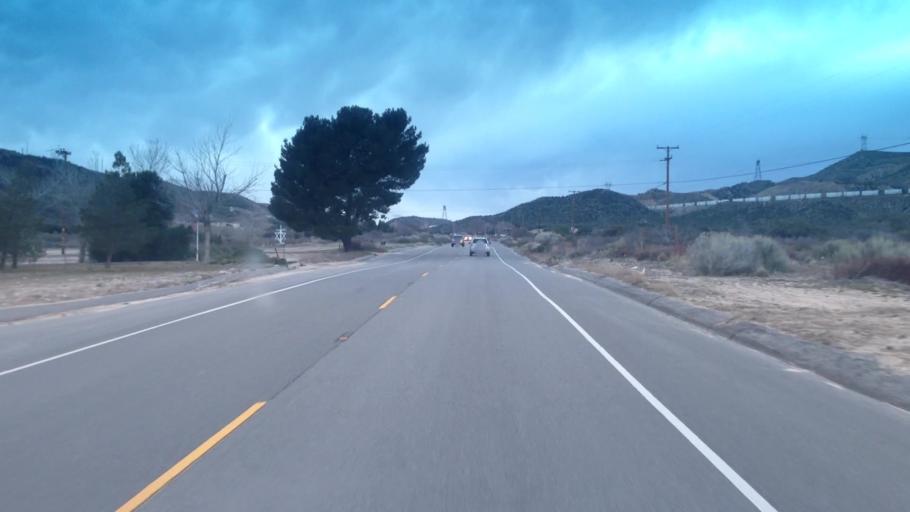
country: US
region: California
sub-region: San Bernardino County
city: Oak Hills
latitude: 34.3234
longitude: -117.4018
